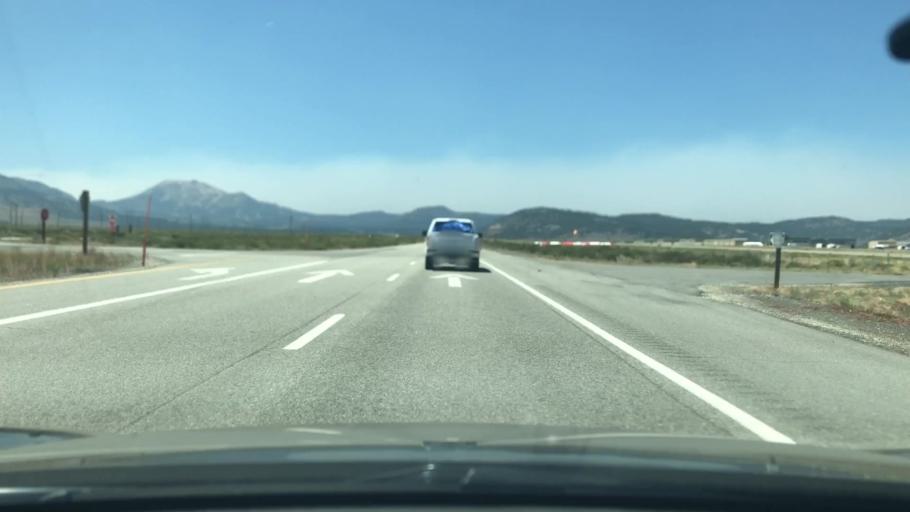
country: US
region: California
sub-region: Mono County
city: Mammoth Lakes
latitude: 37.6228
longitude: -118.8393
